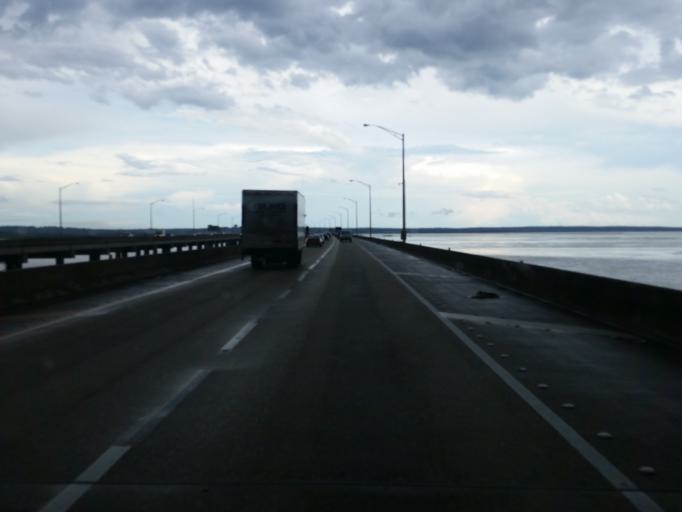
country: US
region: Alabama
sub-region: Baldwin County
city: Spanish Fort
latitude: 30.6690
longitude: -87.9736
